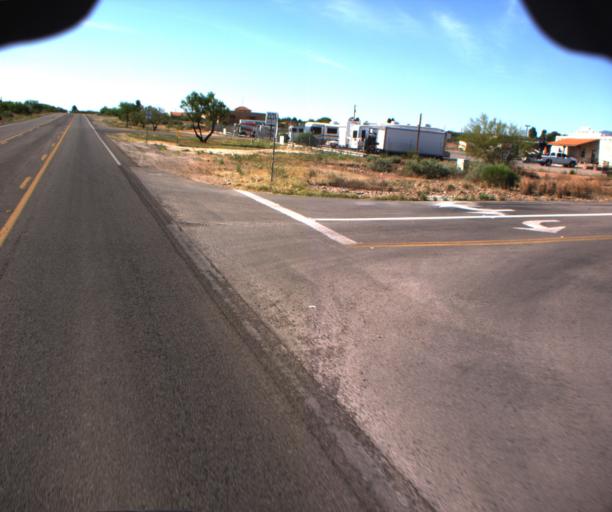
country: US
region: Arizona
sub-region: Cochise County
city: Benson
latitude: 31.9617
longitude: -110.2883
